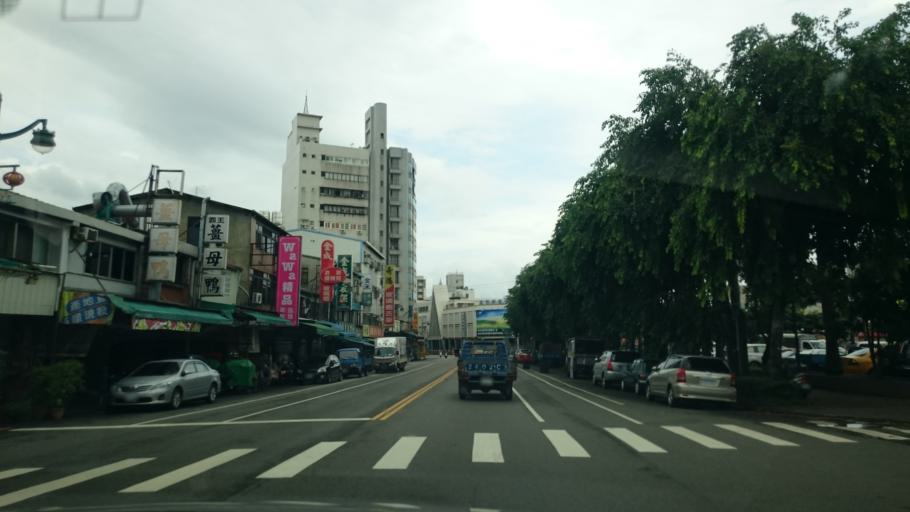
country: TW
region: Taiwan
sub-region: Taichung City
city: Taichung
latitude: 24.1485
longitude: 120.6783
